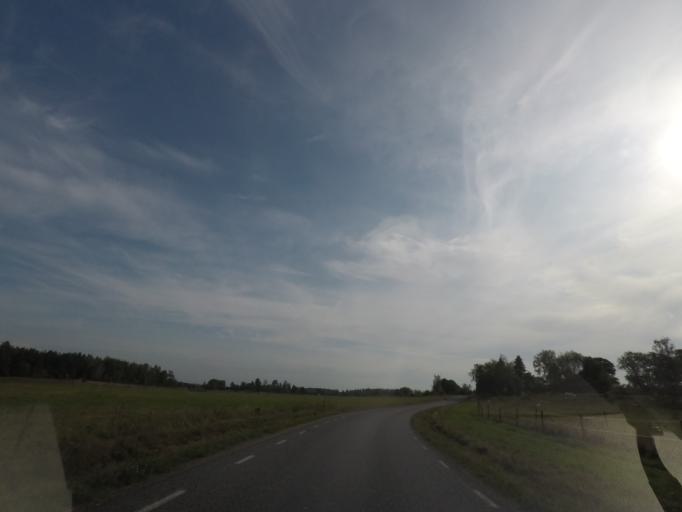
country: SE
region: Vaestmanland
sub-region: Hallstahammars Kommun
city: Kolback
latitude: 59.5292
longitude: 16.1426
